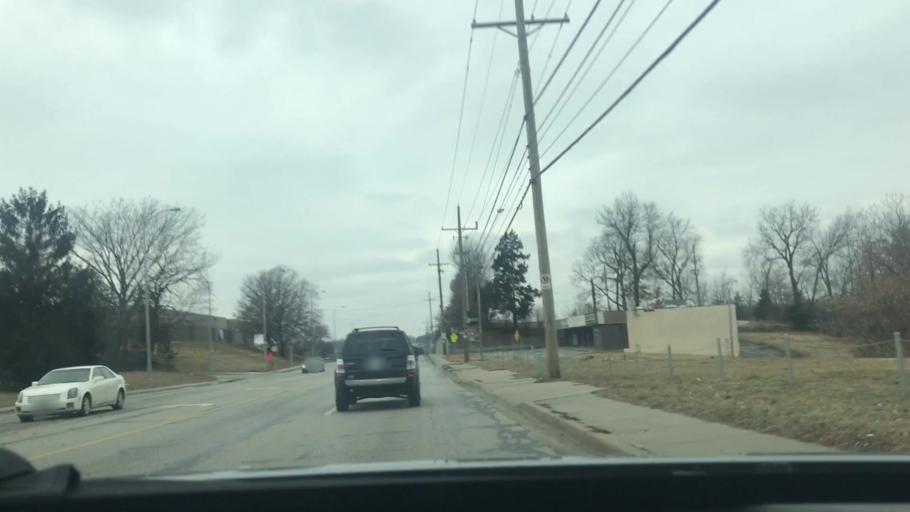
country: US
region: Kansas
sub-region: Johnson County
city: Mission Hills
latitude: 39.0127
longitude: -94.5598
